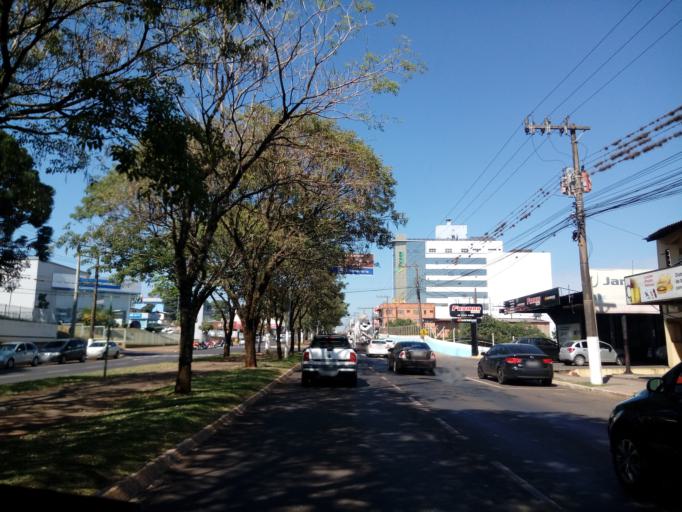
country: BR
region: Santa Catarina
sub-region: Chapeco
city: Chapeco
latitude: -27.0795
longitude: -52.6214
